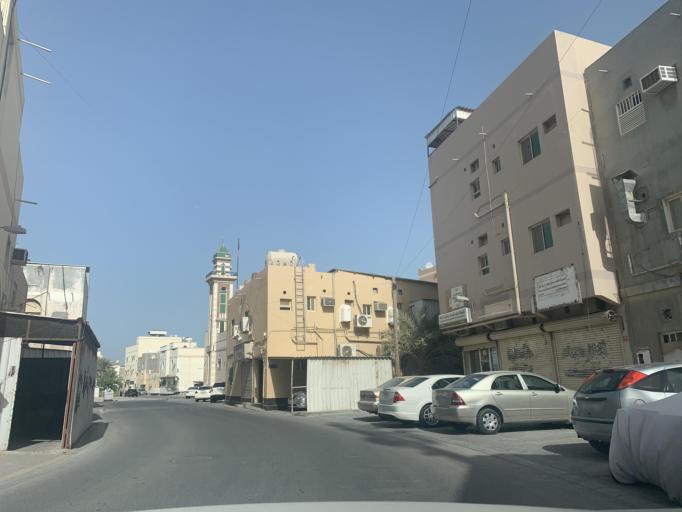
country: BH
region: Northern
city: Sitrah
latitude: 26.1690
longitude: 50.6243
